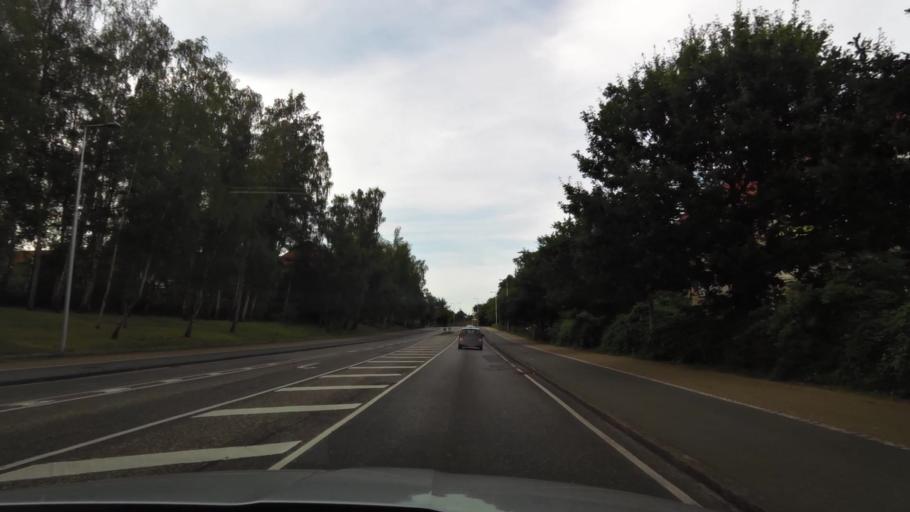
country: DK
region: Capital Region
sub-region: Rudersdal Kommune
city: Birkerod
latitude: 55.8279
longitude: 12.4301
